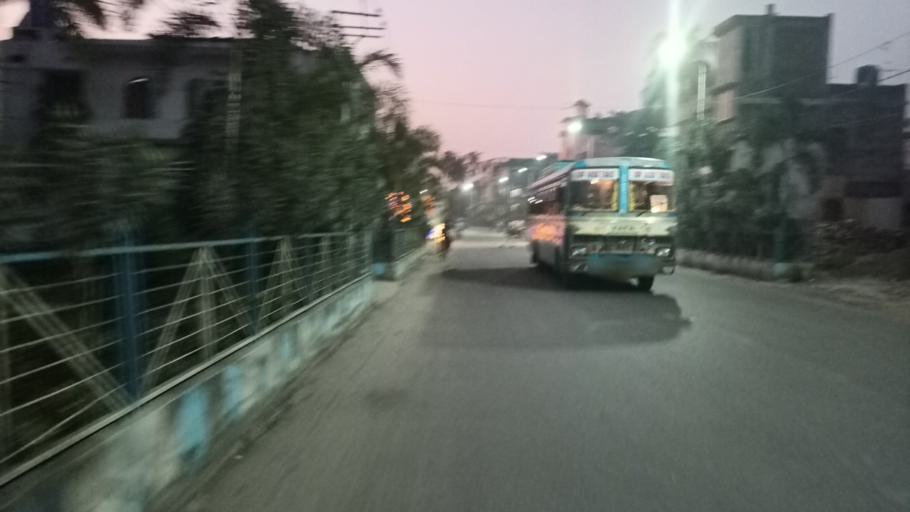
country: IN
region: West Bengal
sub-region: North 24 Parganas
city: Bangaon
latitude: 23.0474
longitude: 88.8369
